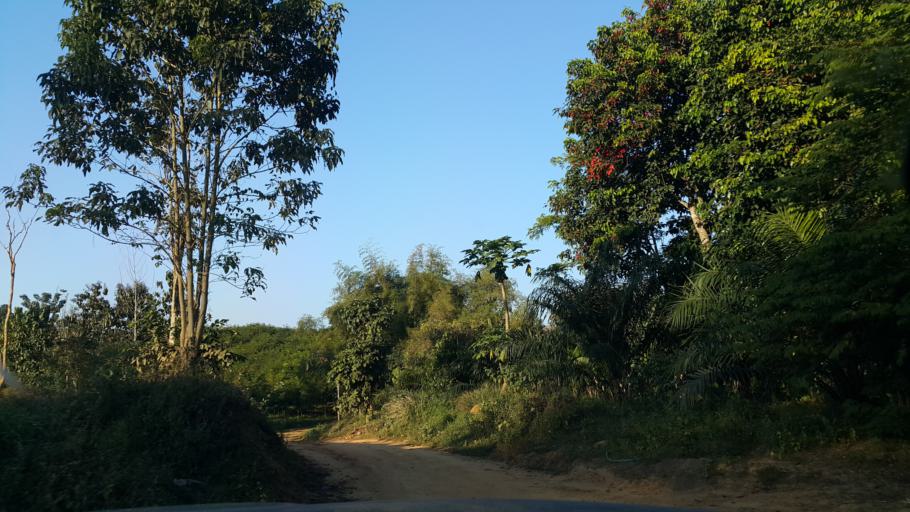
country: TH
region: Sukhothai
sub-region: Amphoe Si Satchanalai
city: Si Satchanalai
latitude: 17.5854
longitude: 99.6096
